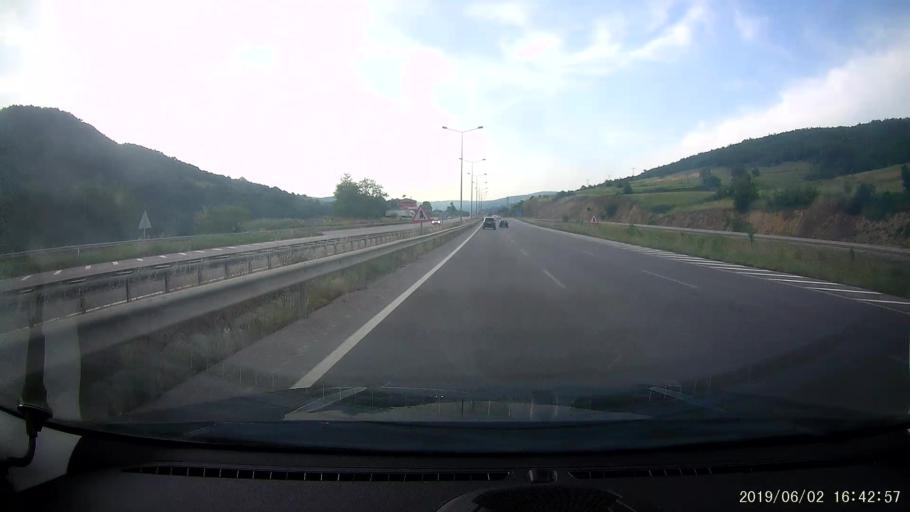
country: TR
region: Samsun
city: Kavak
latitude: 41.1271
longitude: 36.1372
